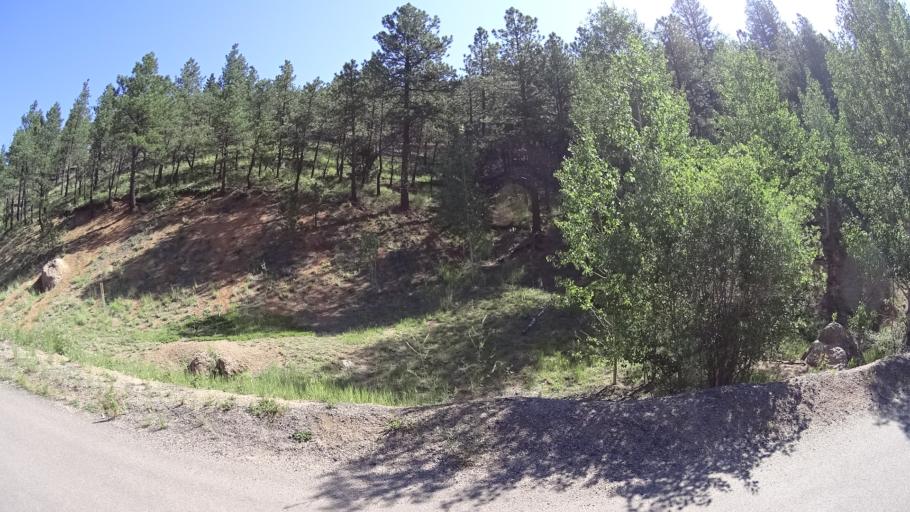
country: US
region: Colorado
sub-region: El Paso County
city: Cascade-Chipita Park
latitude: 38.9085
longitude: -105.0135
